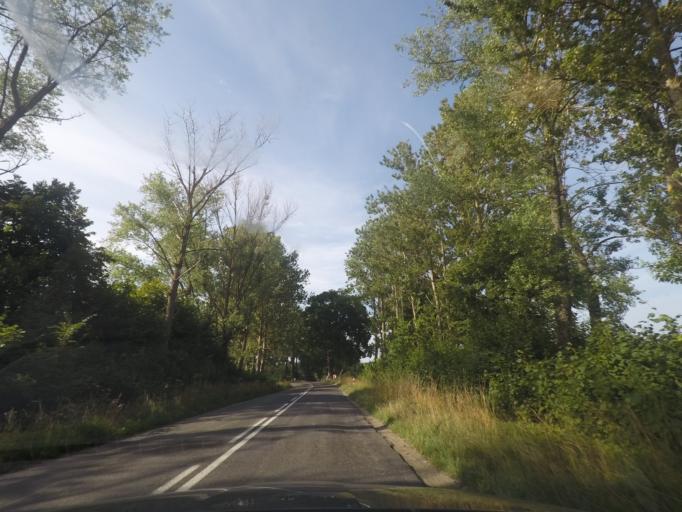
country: PL
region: Pomeranian Voivodeship
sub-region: Powiat leborski
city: Leba
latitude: 54.6877
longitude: 17.5961
